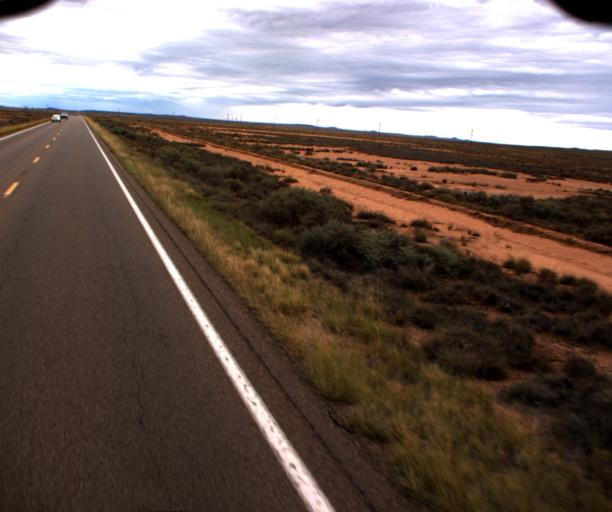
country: US
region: Arizona
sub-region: Navajo County
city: Holbrook
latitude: 34.8066
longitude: -110.1370
